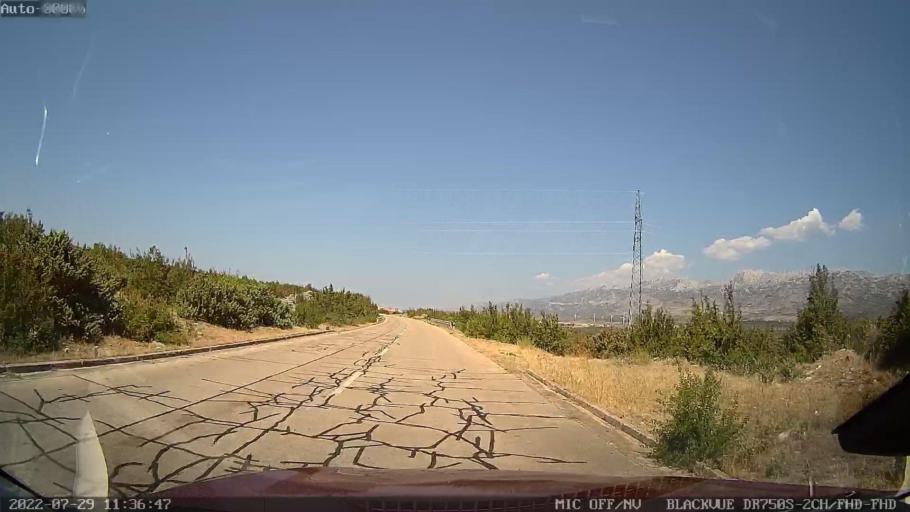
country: HR
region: Zadarska
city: Obrovac
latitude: 44.1919
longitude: 15.6929
